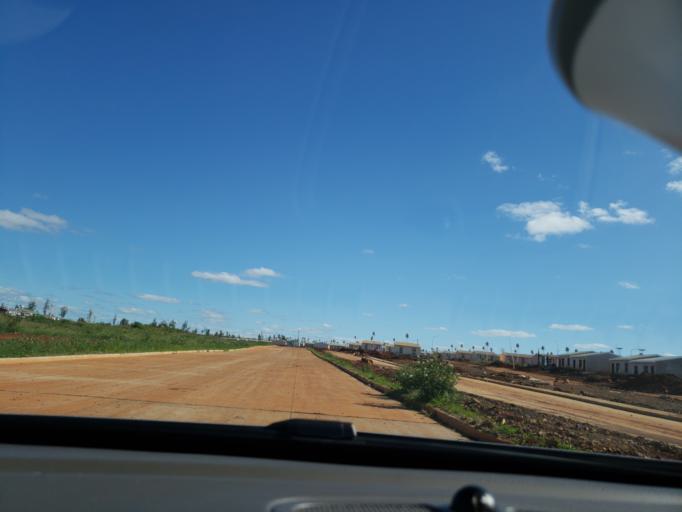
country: AR
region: Misiones
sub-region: Departamento de Capital
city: Posadas
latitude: -27.4094
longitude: -55.9890
